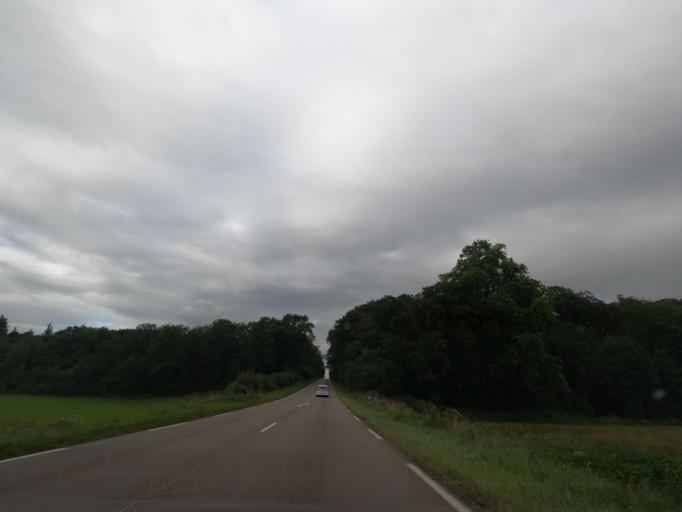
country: FR
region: Haute-Normandie
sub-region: Departement de l'Eure
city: Bourgtheroulde-Infreville
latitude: 49.2780
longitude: 0.8293
